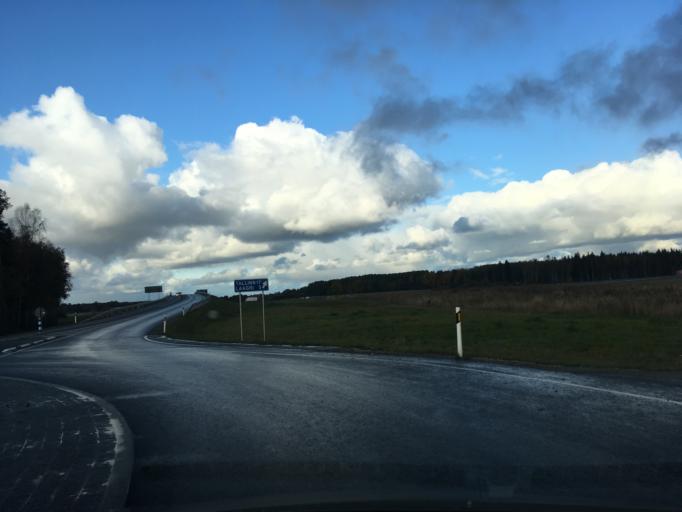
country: EE
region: Harju
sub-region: Saku vald
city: Saku
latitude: 59.3136
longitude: 24.6410
